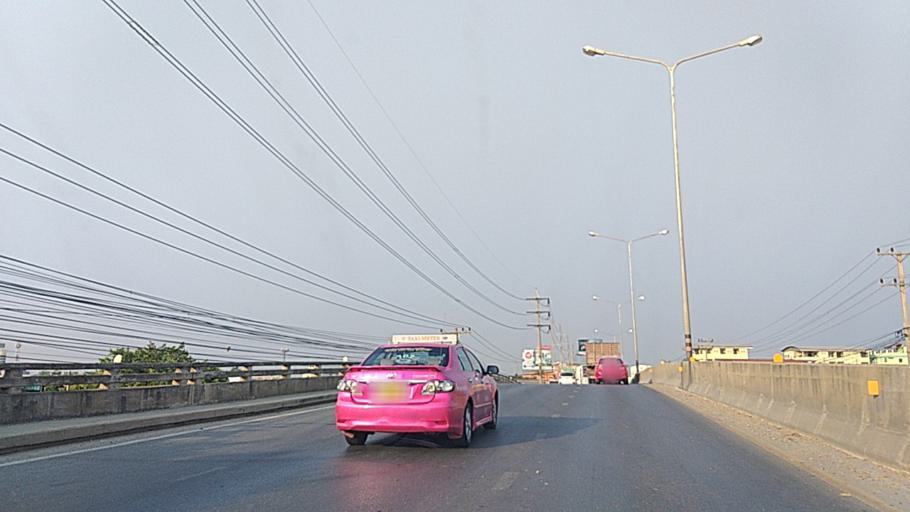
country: TH
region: Phra Nakhon Si Ayutthaya
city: Ban Bang Kadi Pathum Thani
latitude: 13.9950
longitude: 100.5524
